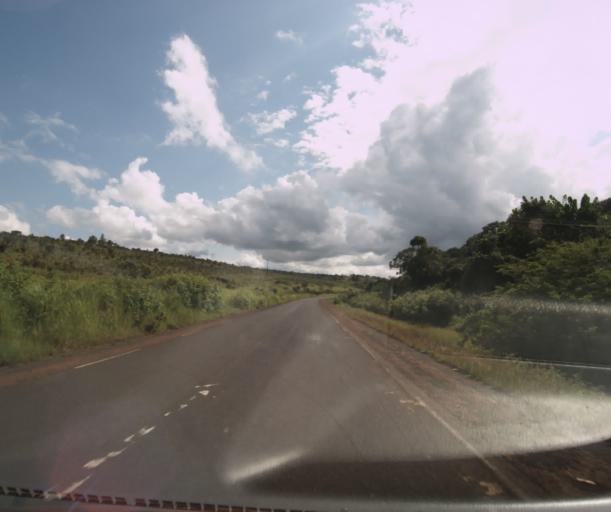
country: CM
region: West
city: Foumban
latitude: 5.6996
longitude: 10.8255
